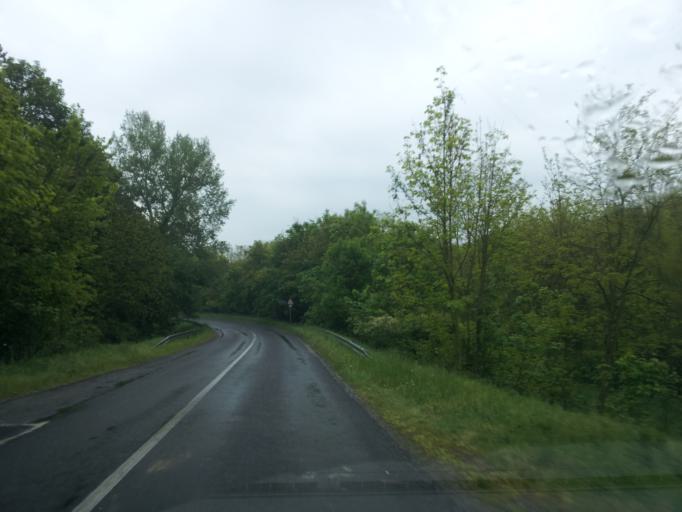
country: HU
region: Tolna
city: Bonyhad
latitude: 46.2557
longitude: 18.6027
